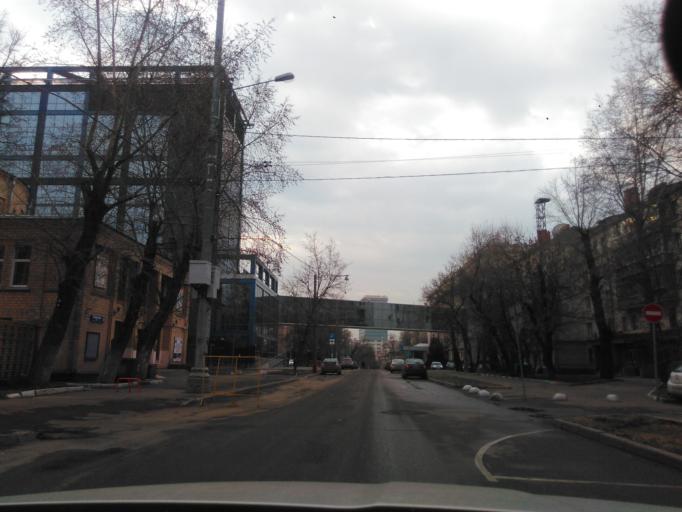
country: RU
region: Moskovskaya
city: Dorogomilovo
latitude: 55.7887
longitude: 37.5770
